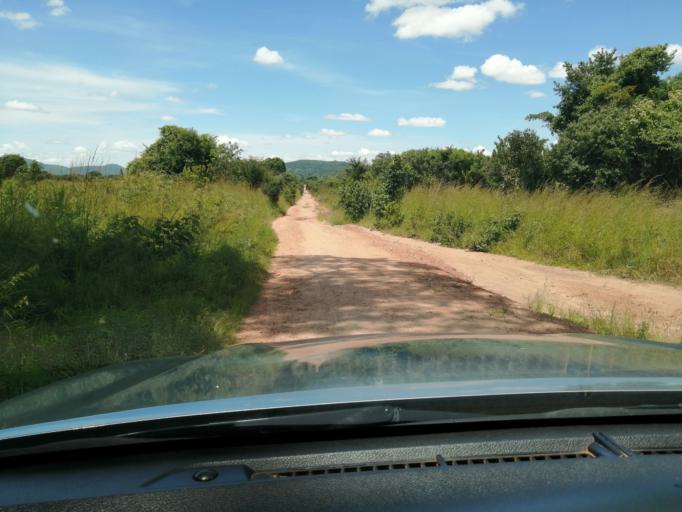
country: ZM
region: Lusaka
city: Lusaka
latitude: -15.1311
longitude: 27.8967
